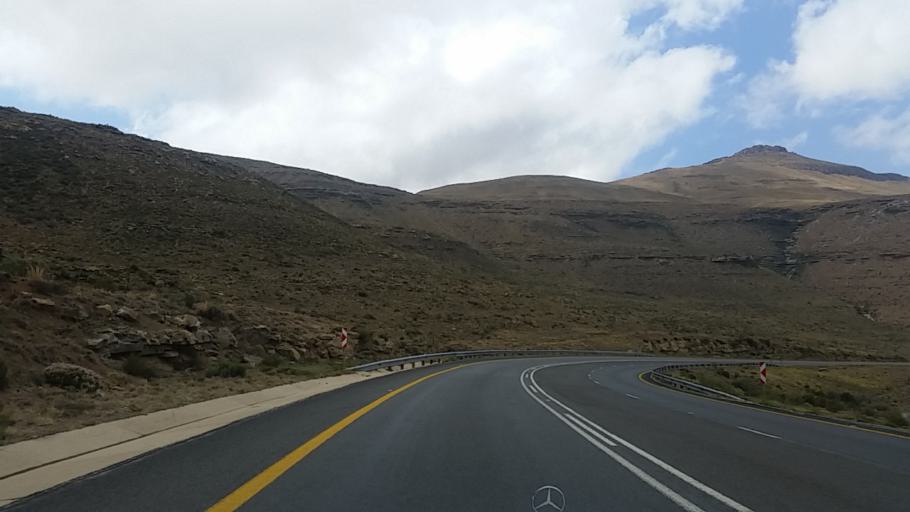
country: ZA
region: Eastern Cape
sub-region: Chris Hani District Municipality
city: Middelburg
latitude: -31.8441
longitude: 24.8756
